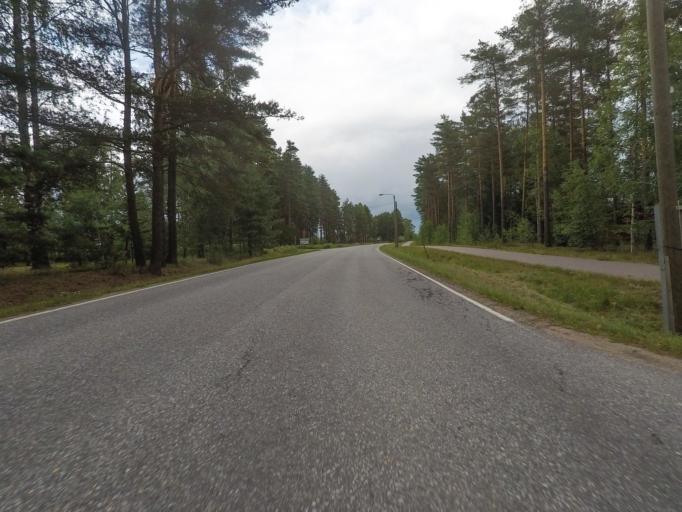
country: FI
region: Varsinais-Suomi
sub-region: Salo
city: Muurla
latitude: 60.3665
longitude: 23.2993
